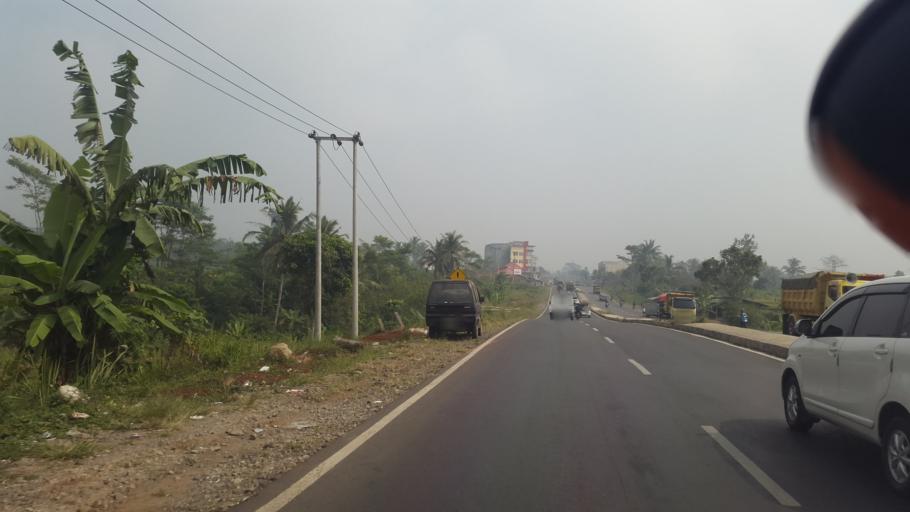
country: ID
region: West Java
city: Sukabumi
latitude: -6.9285
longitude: 106.8981
